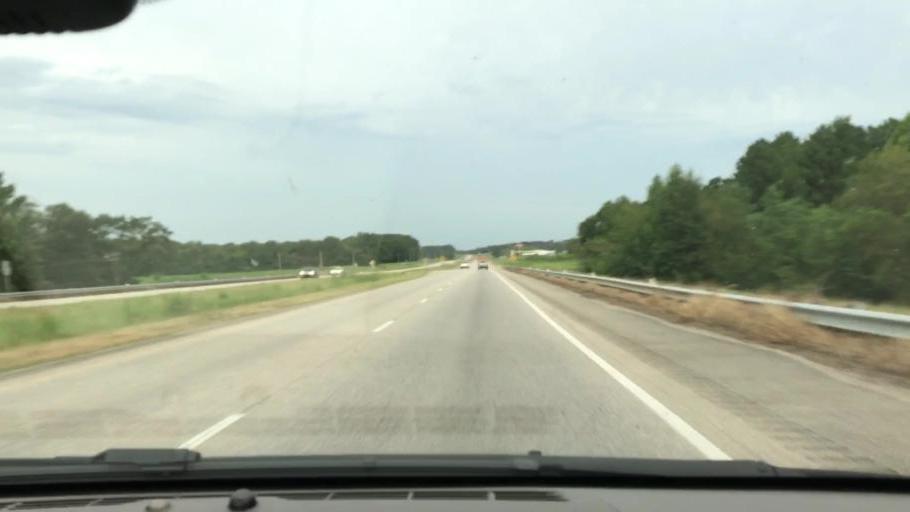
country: US
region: Alabama
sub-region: Houston County
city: Ashford
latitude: 31.1765
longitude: -85.2399
